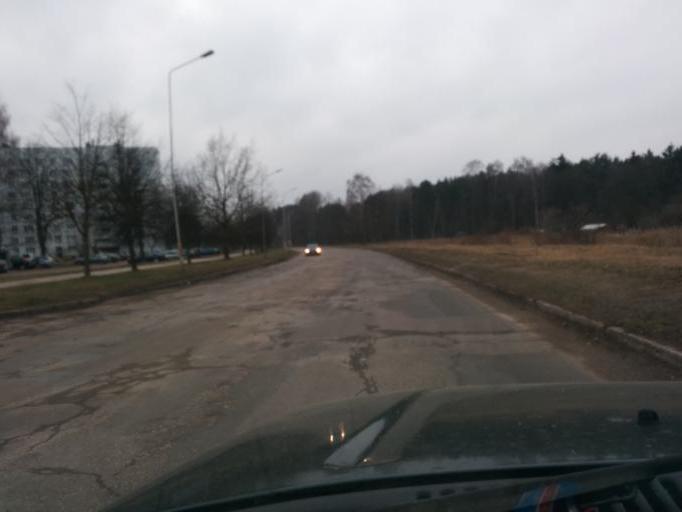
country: LV
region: Ozolnieku
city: Ozolnieki
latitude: 56.6712
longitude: 23.7585
